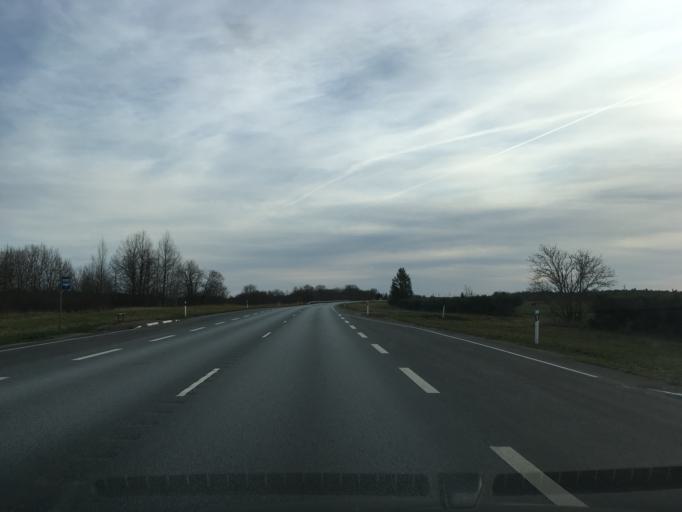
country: EE
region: Ida-Virumaa
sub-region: Aseri vald
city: Aseri
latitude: 59.4378
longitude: 26.8868
